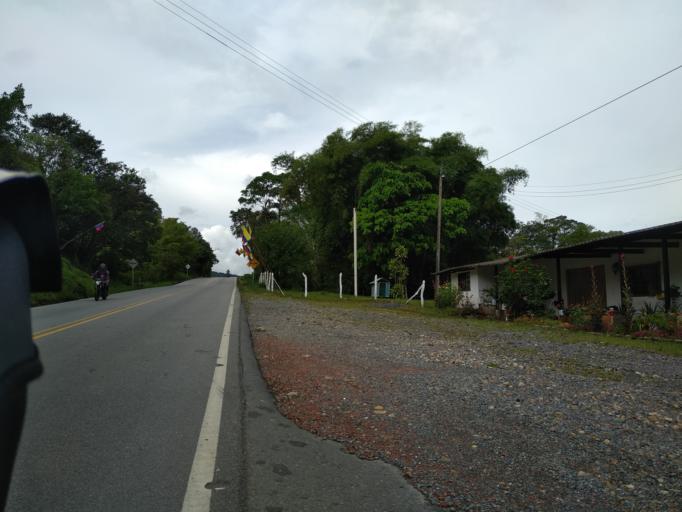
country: CO
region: Santander
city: Suaita
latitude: 6.0918
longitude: -73.3849
